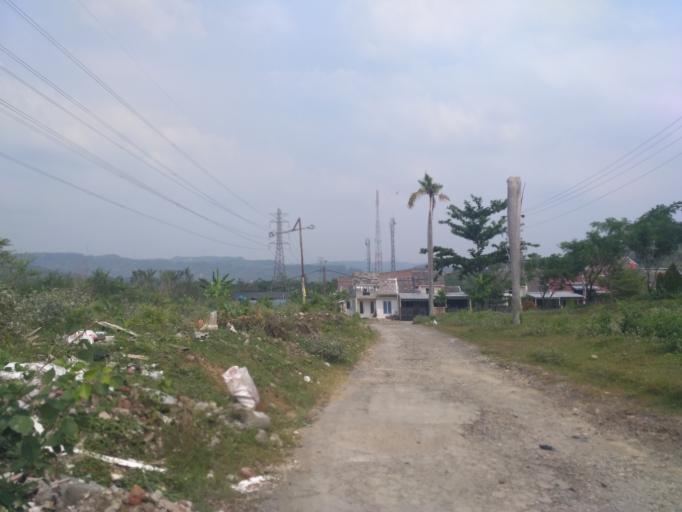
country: ID
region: Central Java
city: Mranggen
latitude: -7.0669
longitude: 110.4612
